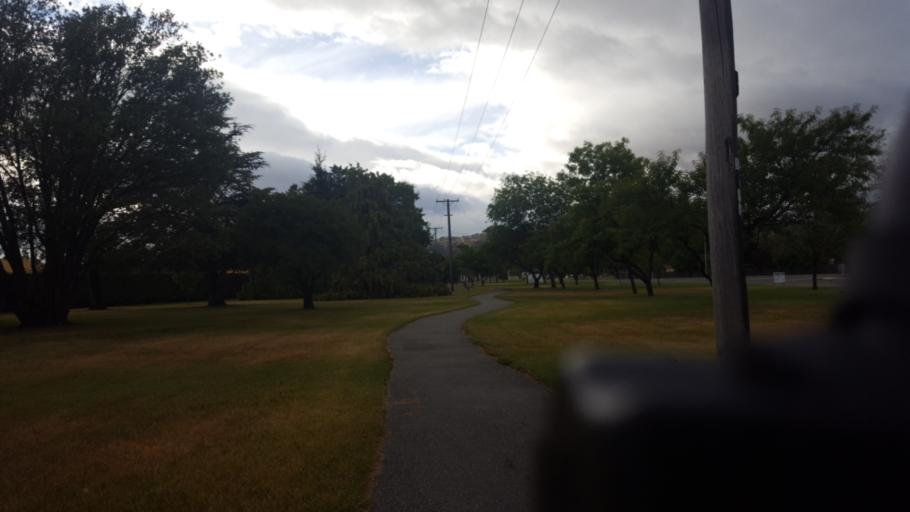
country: NZ
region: Otago
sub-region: Queenstown-Lakes District
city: Wanaka
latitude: -45.2444
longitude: 169.3799
